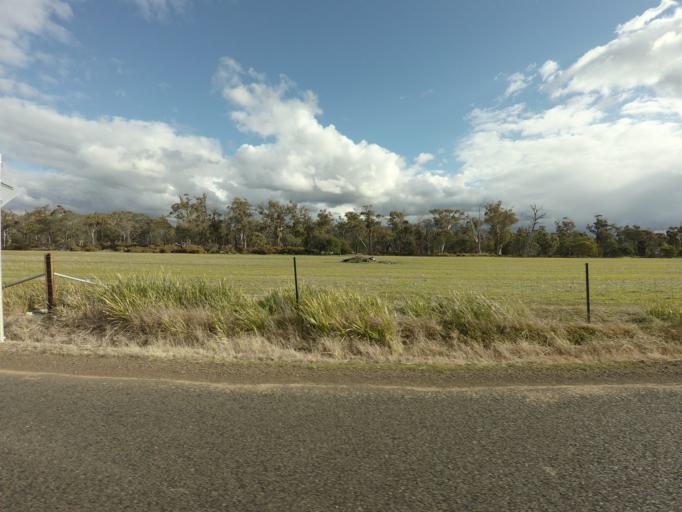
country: AU
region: Tasmania
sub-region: Northern Midlands
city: Evandale
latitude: -41.8625
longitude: 147.2641
